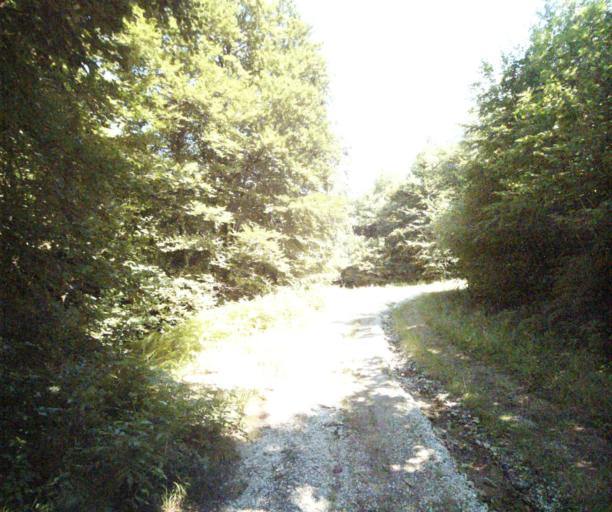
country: FR
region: Midi-Pyrenees
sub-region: Departement du Tarn
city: Soreze
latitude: 43.4385
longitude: 2.1030
